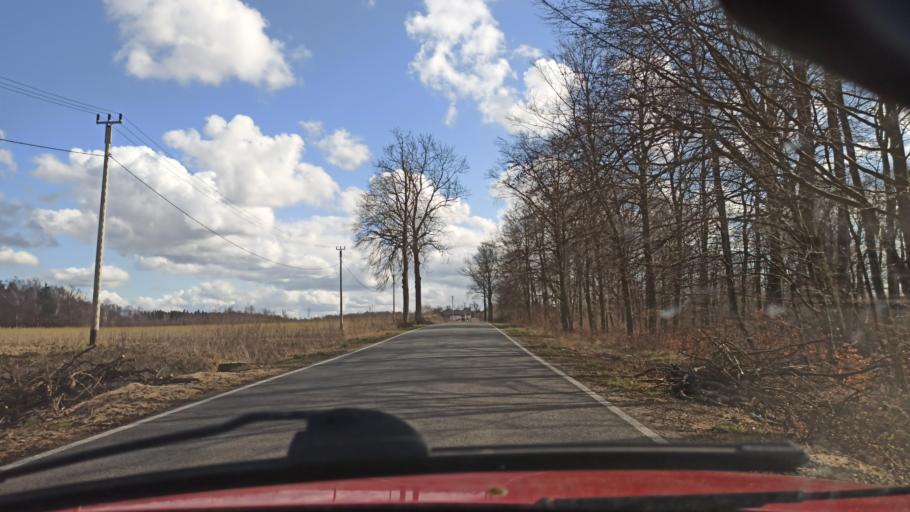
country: PL
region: Warmian-Masurian Voivodeship
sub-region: Powiat elblaski
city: Tolkmicko
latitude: 54.2751
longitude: 19.4838
